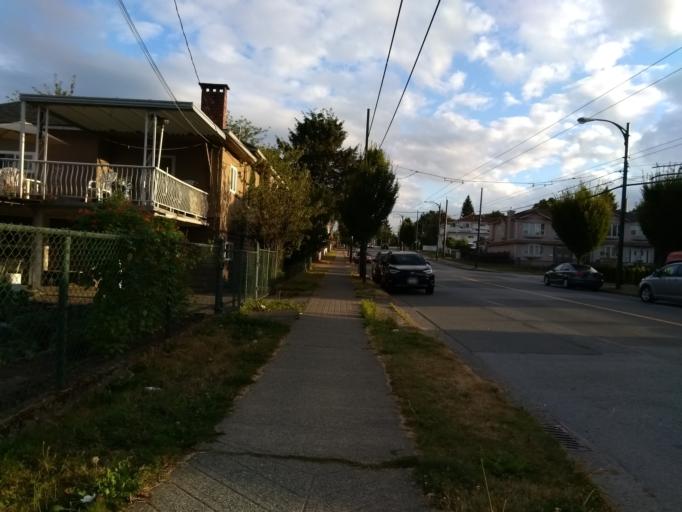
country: CA
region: British Columbia
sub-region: Fraser Valley Regional District
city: North Vancouver
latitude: 49.2467
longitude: -123.0416
